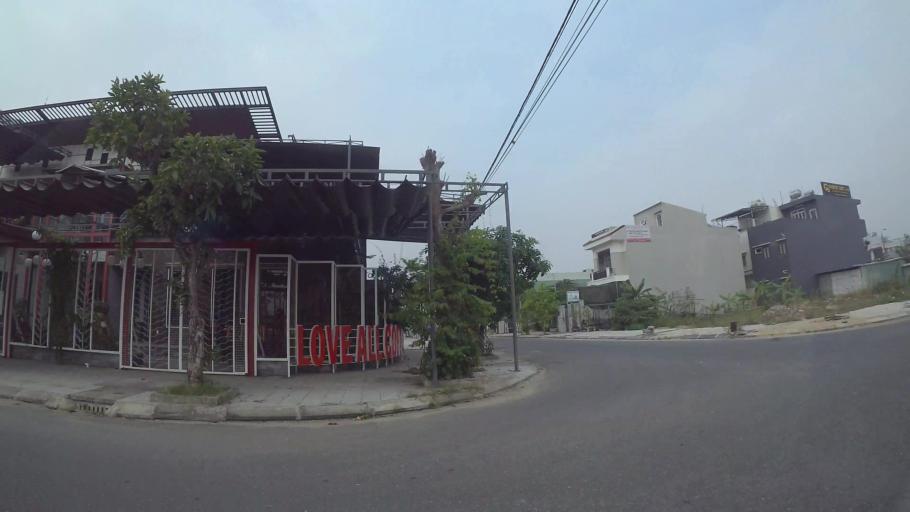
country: VN
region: Da Nang
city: Cam Le
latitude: 16.0127
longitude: 108.2236
